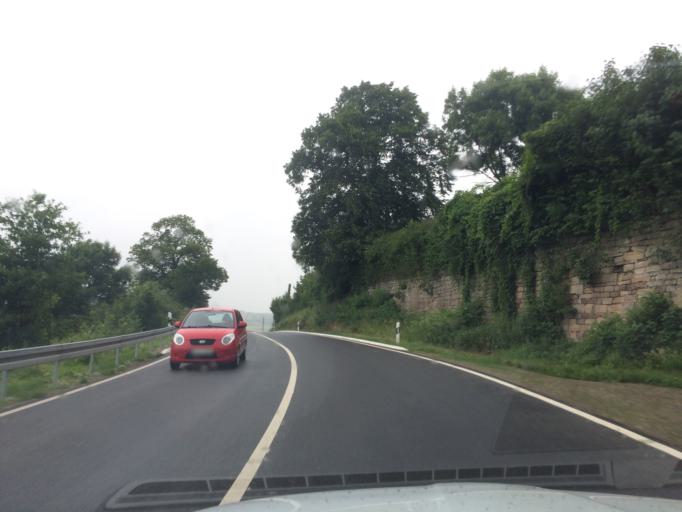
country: DE
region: Hesse
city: Trendelburg
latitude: 51.5863
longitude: 9.4151
